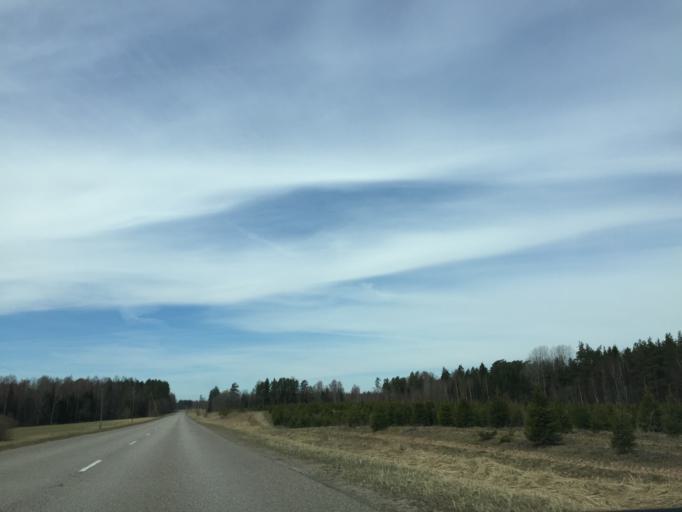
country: LV
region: Valkas Rajons
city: Valka
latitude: 57.7922
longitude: 25.8795
